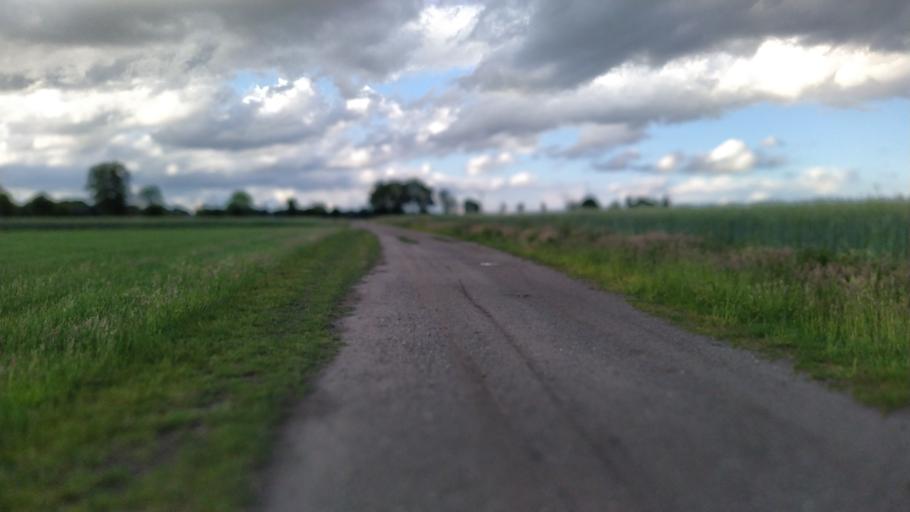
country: DE
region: Lower Saxony
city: Kutenholz
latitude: 53.4590
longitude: 9.3451
